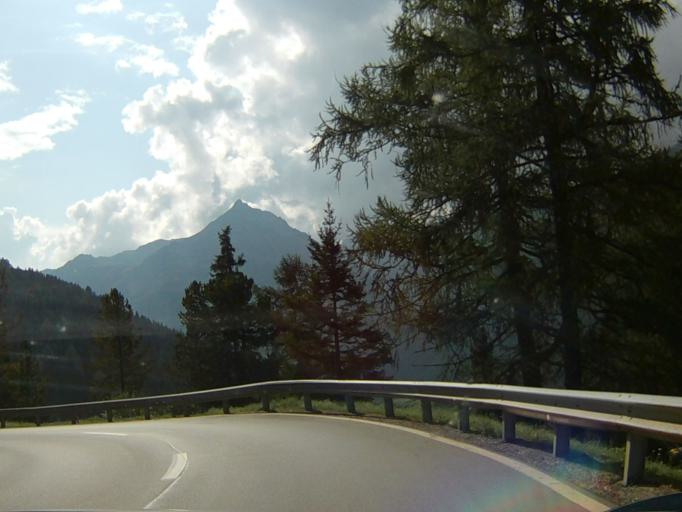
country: CH
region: Grisons
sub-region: Maloja District
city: Silvaplana
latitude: 46.3958
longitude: 9.6930
